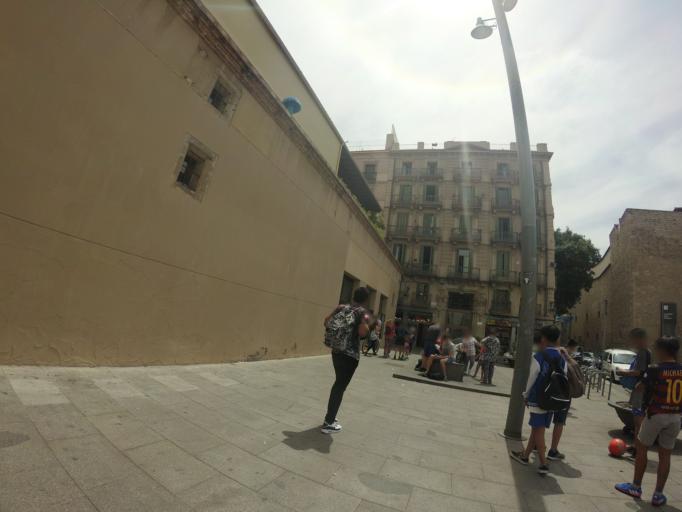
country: ES
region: Catalonia
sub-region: Provincia de Barcelona
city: Ciutat Vella
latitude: 41.3829
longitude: 2.1678
